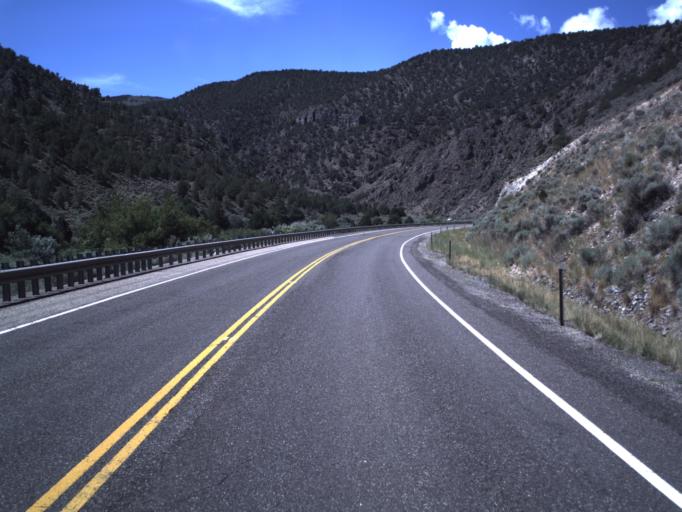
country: US
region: Utah
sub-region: Piute County
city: Junction
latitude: 38.1222
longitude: -112.3332
